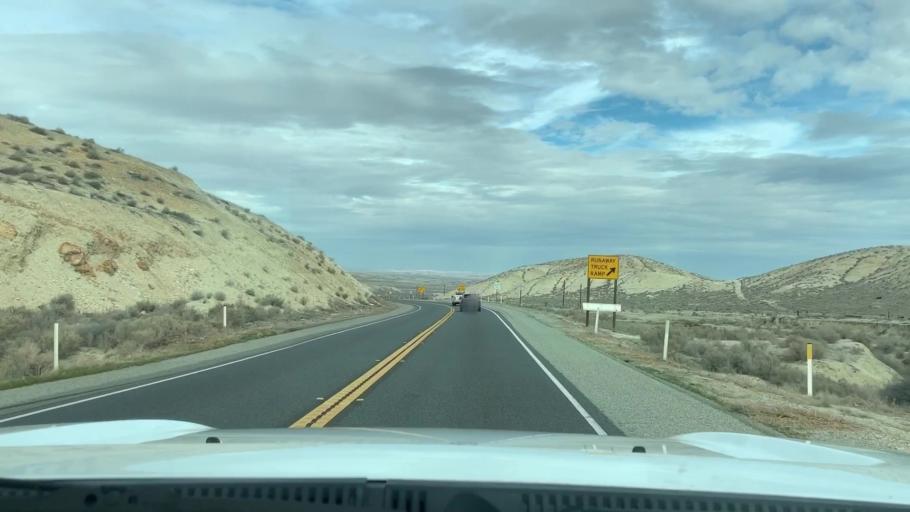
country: US
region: California
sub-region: Kern County
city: Maricopa
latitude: 35.0324
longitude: -119.4192
